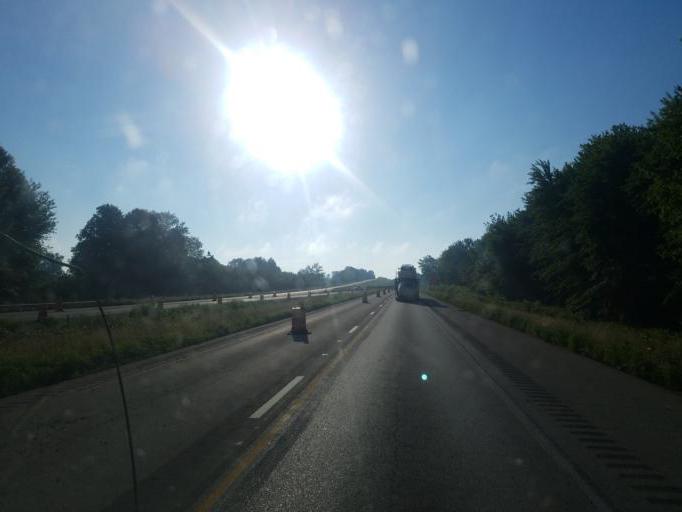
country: US
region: Illinois
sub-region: Fayette County
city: Vandalia
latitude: 38.9753
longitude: -89.0372
